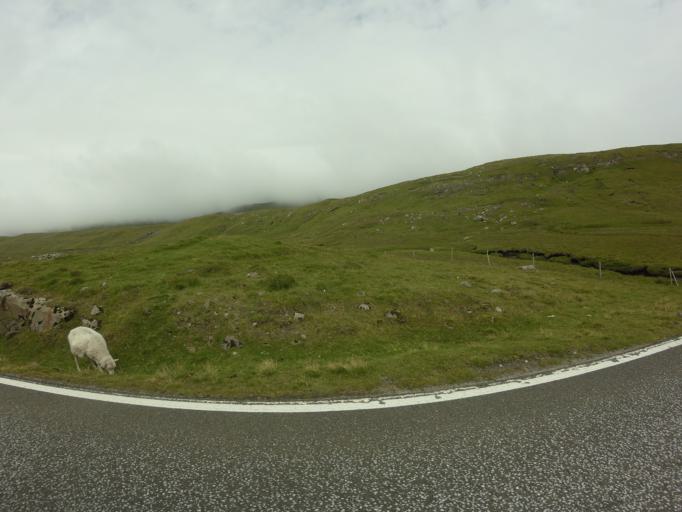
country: FO
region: Sandoy
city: Sandur
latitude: 61.8285
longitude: -6.7571
